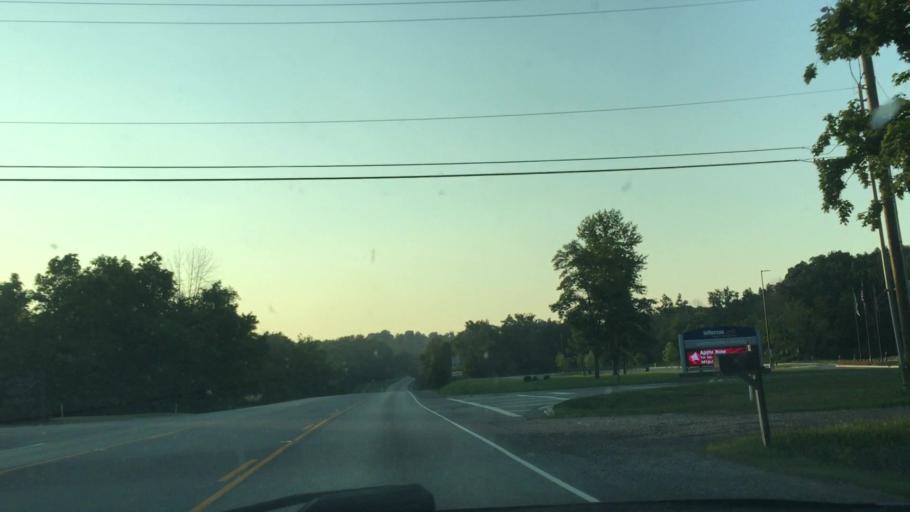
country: US
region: Kentucky
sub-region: Carroll County
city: Carrollton
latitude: 38.6667
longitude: -85.1436
